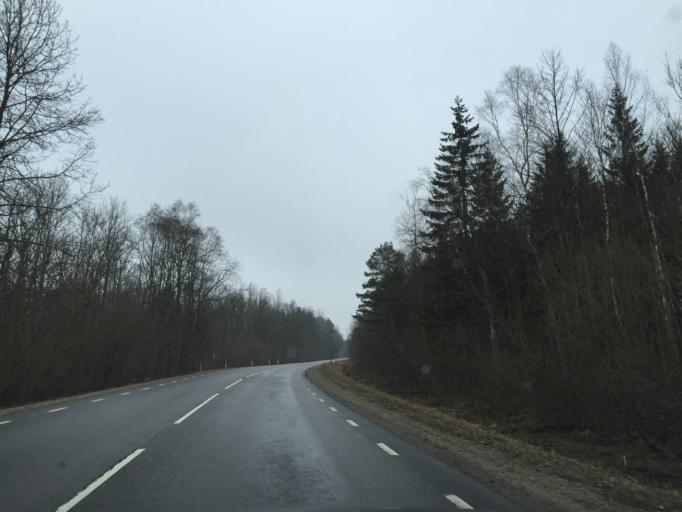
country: EE
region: Laeaene
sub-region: Lihula vald
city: Lihula
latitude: 58.6072
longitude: 23.6963
